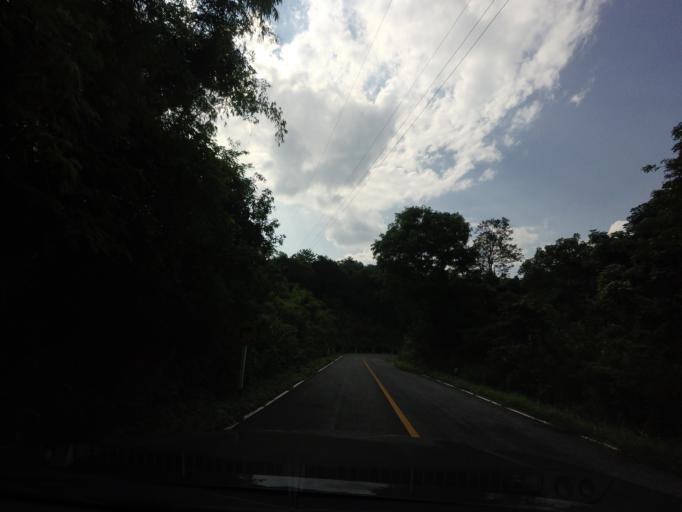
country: TH
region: Uttaradit
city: Ban Khok
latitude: 18.2177
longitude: 101.0340
